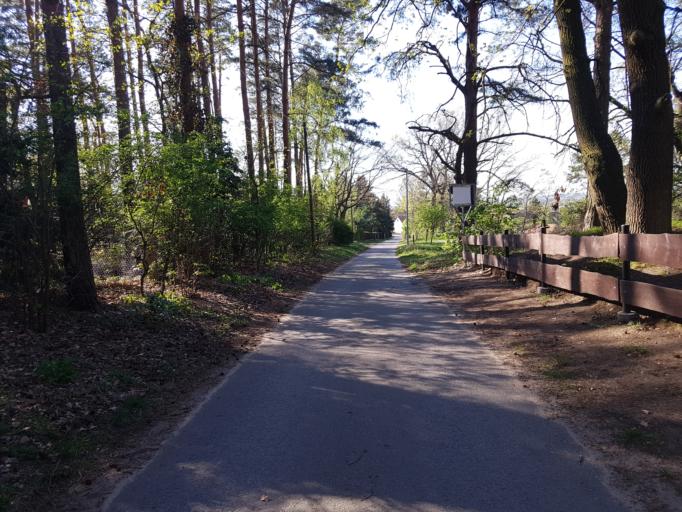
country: DE
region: Brandenburg
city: Groden
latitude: 51.4012
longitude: 13.5723
